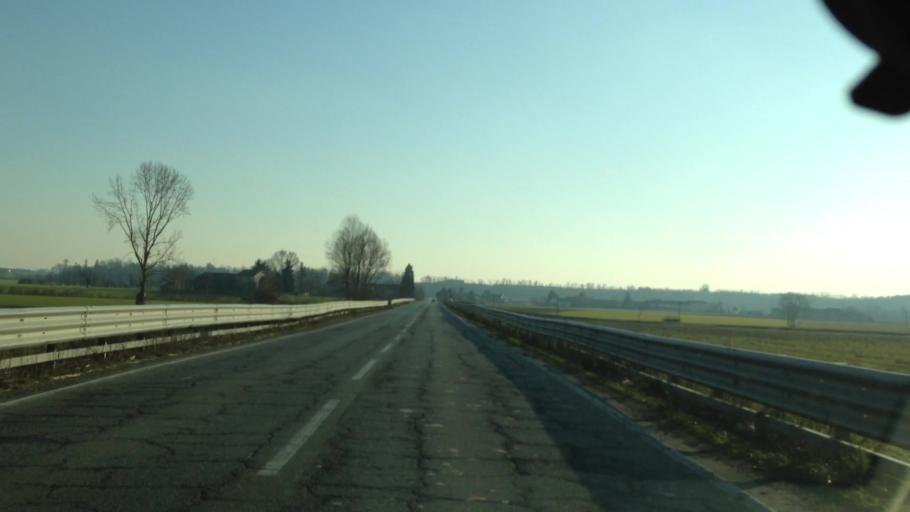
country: IT
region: Piedmont
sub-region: Provincia di Alessandria
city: Felizzano
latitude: 44.8856
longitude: 8.4413
